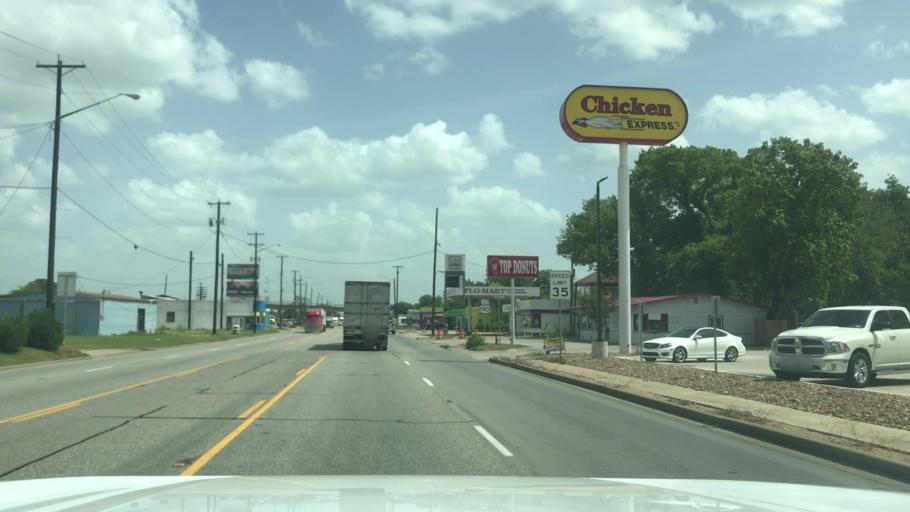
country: US
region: Texas
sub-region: Robertson County
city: Hearne
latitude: 30.8806
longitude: -96.5945
